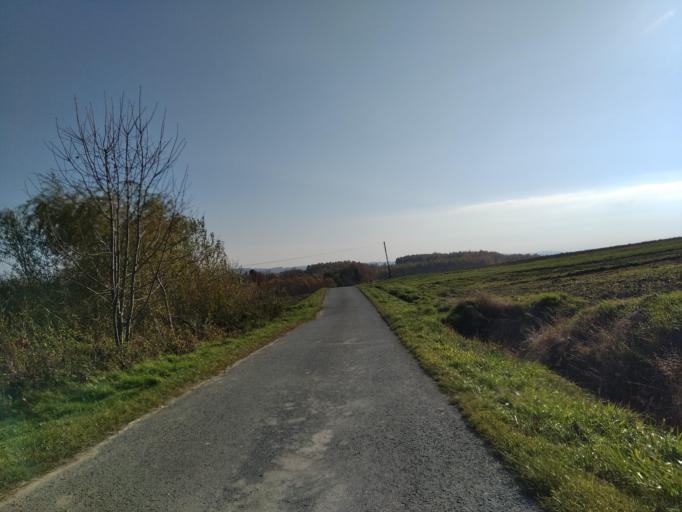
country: PL
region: Subcarpathian Voivodeship
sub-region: Powiat strzyzowski
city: Polomia
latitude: 49.8818
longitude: 21.8830
